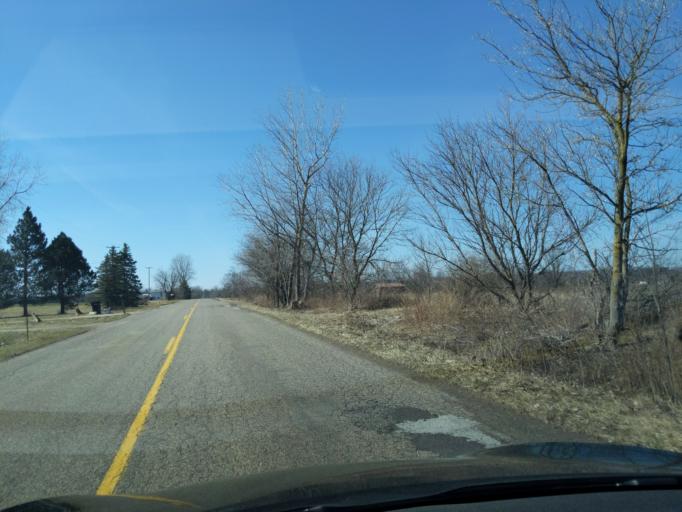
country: US
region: Michigan
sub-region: Ionia County
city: Portland
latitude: 42.7267
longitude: -84.9691
